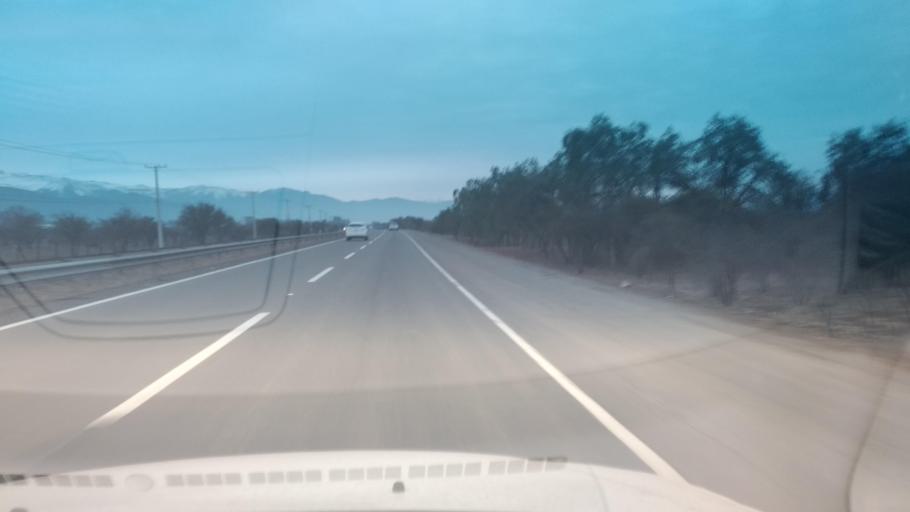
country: CL
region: Santiago Metropolitan
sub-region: Provincia de Chacabuco
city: Chicureo Abajo
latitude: -33.1274
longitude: -70.6729
